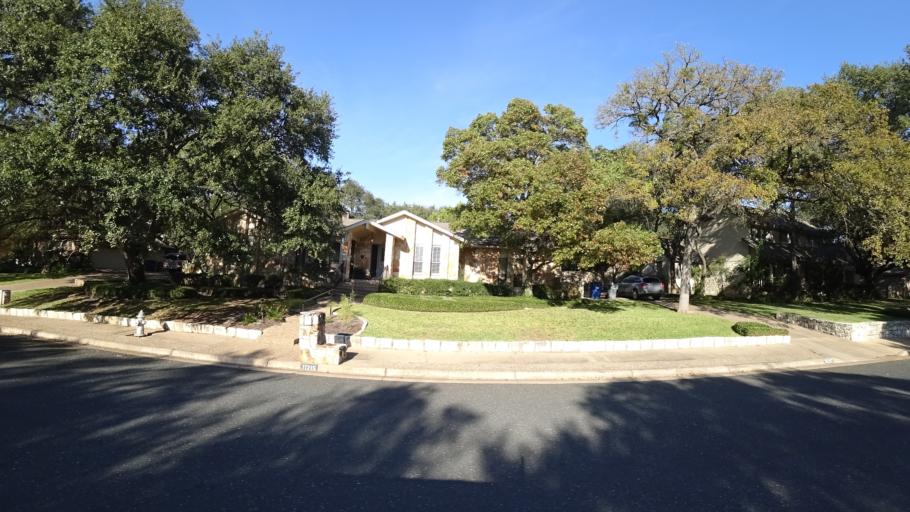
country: US
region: Texas
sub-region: Williamson County
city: Anderson Mill
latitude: 30.4427
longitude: -97.8113
